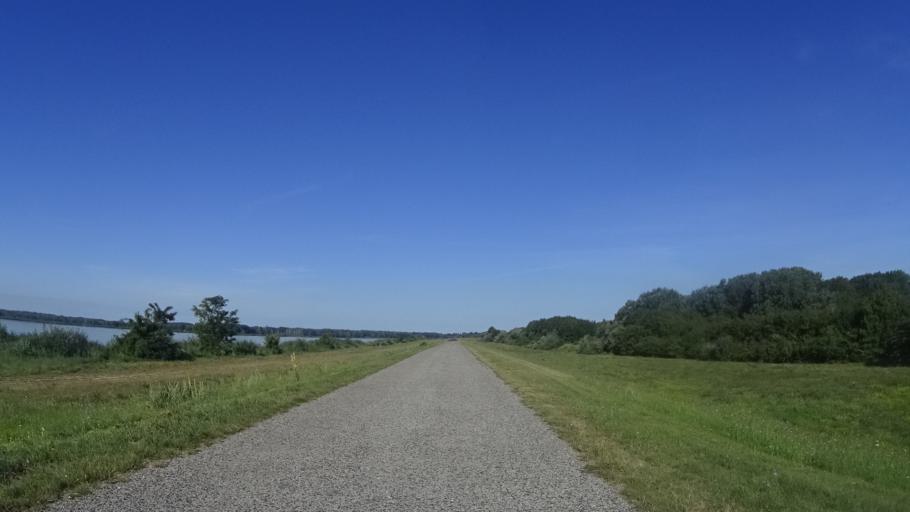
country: SK
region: Bratislavsky
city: Dunajska Luzna
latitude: 48.0596
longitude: 17.2106
